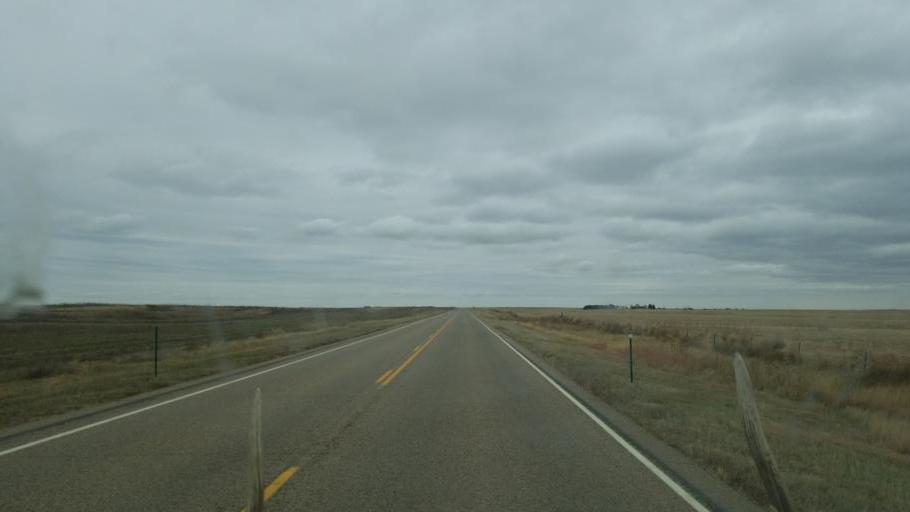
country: US
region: Colorado
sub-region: Cheyenne County
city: Cheyenne Wells
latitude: 38.8349
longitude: -102.2884
